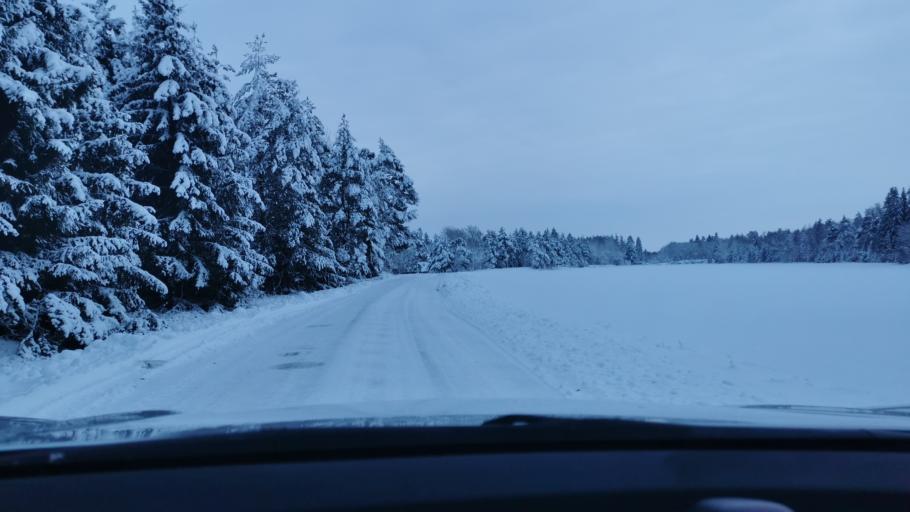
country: EE
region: Laeaene-Virumaa
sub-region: Haljala vald
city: Haljala
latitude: 59.5013
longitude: 26.3029
